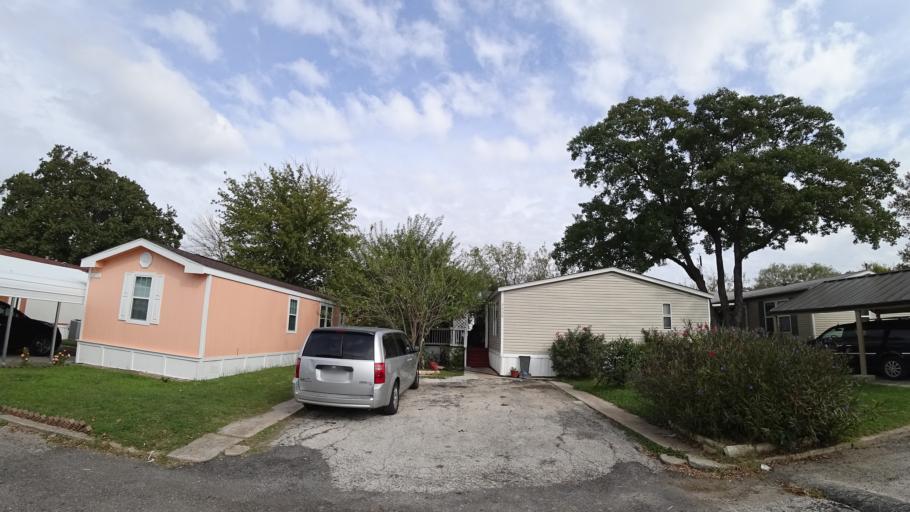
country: US
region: Texas
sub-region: Williamson County
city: Round Rock
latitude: 30.4855
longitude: -97.6916
